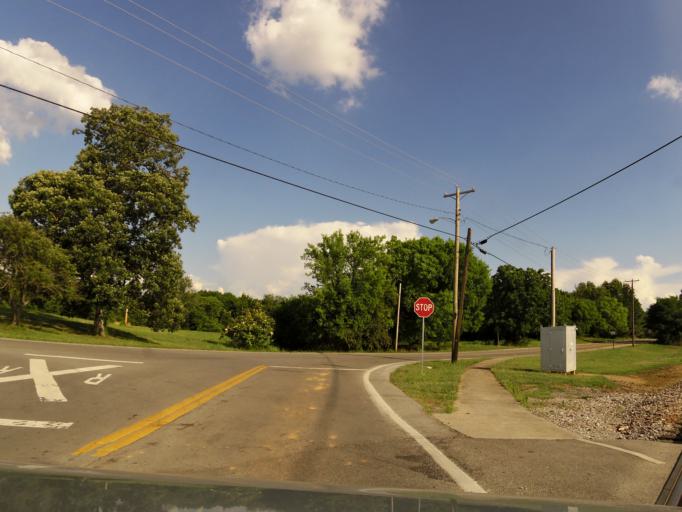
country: US
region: Tennessee
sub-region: Blount County
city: Alcoa
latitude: 35.7787
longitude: -83.9663
